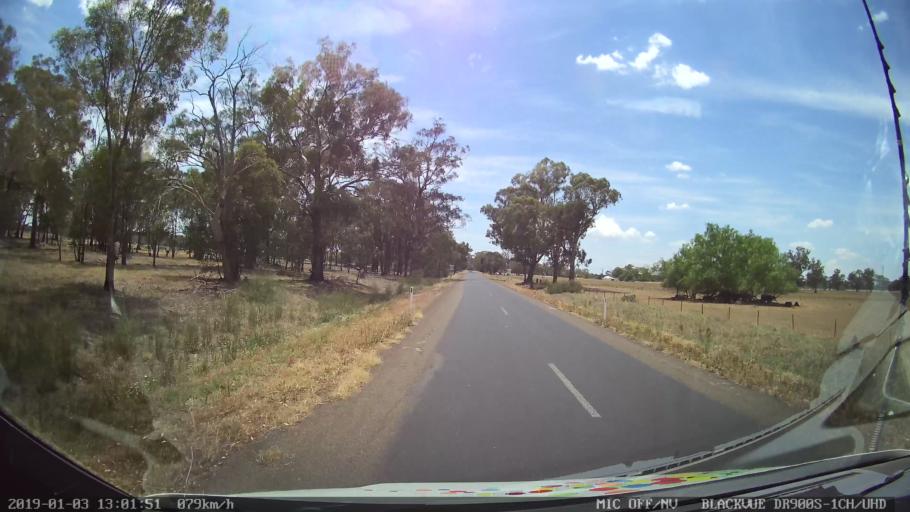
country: AU
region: New South Wales
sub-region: Cabonne
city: Canowindra
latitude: -33.6212
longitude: 148.4234
